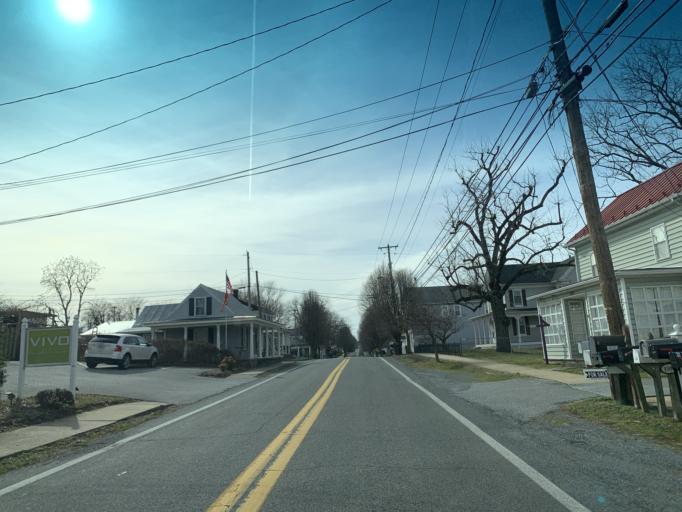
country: US
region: West Virginia
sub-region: Jefferson County
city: Bolivar
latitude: 39.3254
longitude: -77.7495
